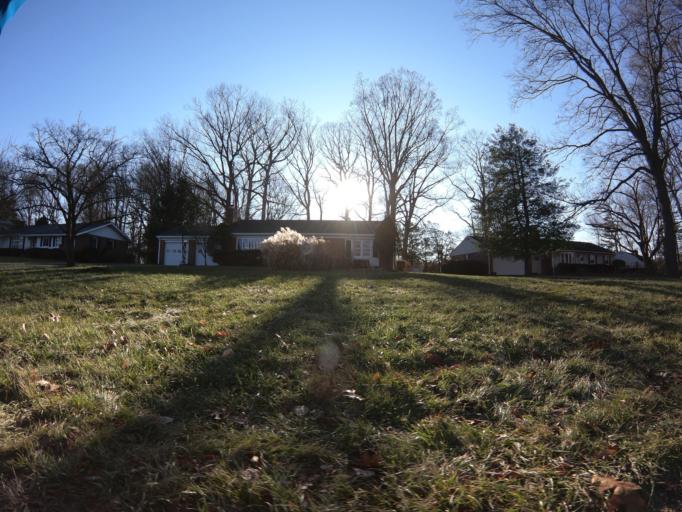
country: US
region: Maryland
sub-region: Howard County
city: Columbia
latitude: 39.2525
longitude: -76.8660
